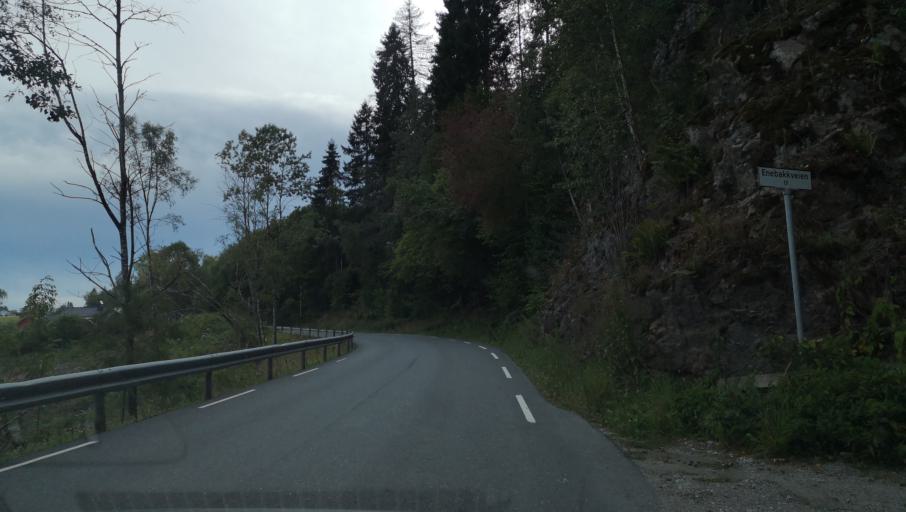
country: NO
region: Ostfold
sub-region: Hobol
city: Tomter
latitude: 59.6646
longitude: 11.0080
